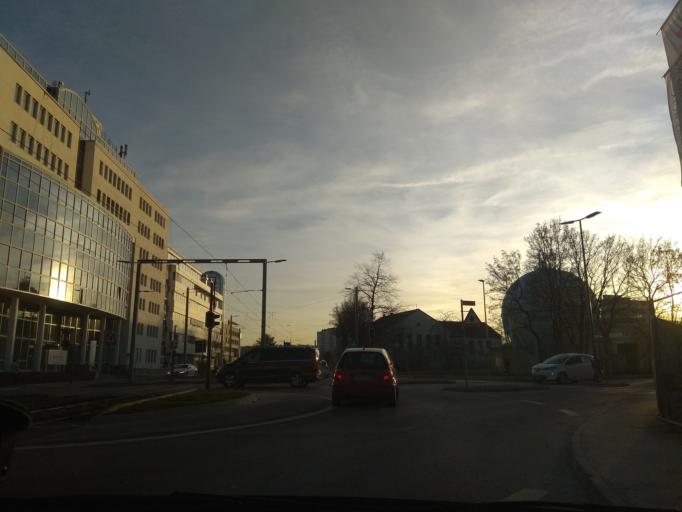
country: DE
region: Baden-Wuerttemberg
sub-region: Regierungsbezirk Stuttgart
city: Leinfelden-Echterdingen
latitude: 48.7243
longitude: 9.1223
